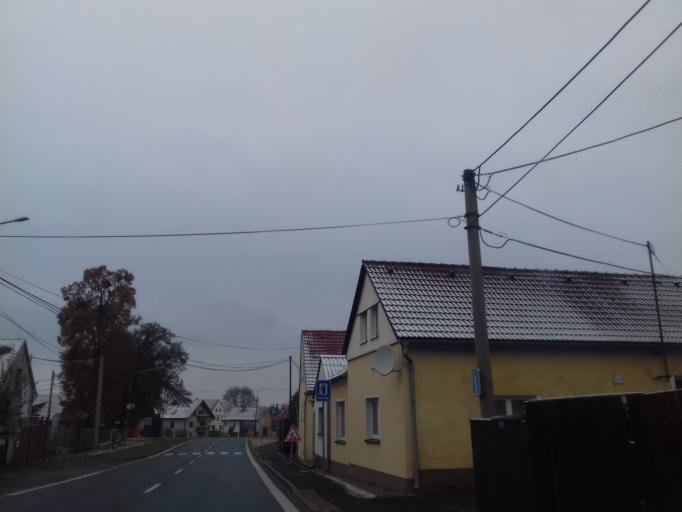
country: CZ
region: Plzensky
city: Meclov
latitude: 49.4552
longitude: 12.8725
